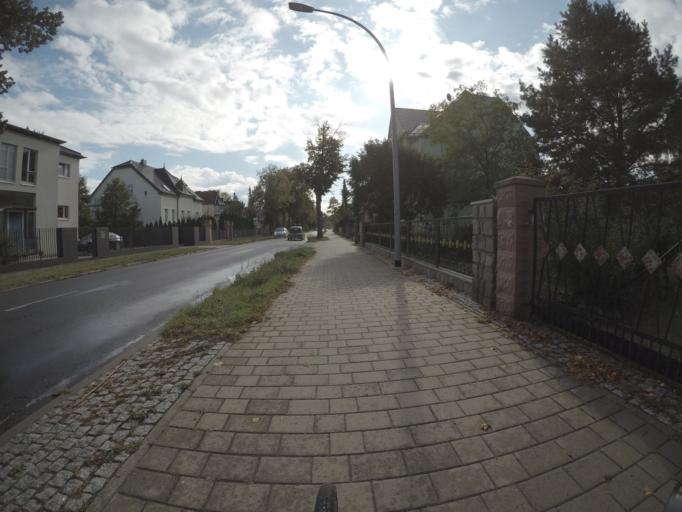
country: DE
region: Brandenburg
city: Rehfelde
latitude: 52.5337
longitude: 13.8455
